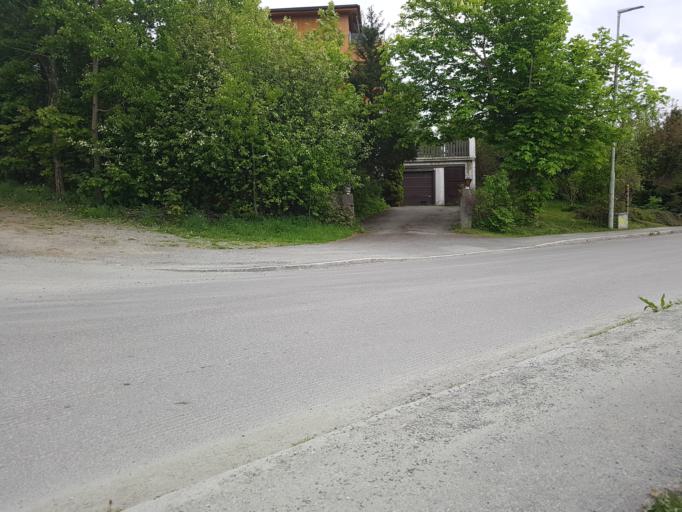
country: NO
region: Sor-Trondelag
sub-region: Trondheim
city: Trondheim
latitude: 63.4295
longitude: 10.4316
